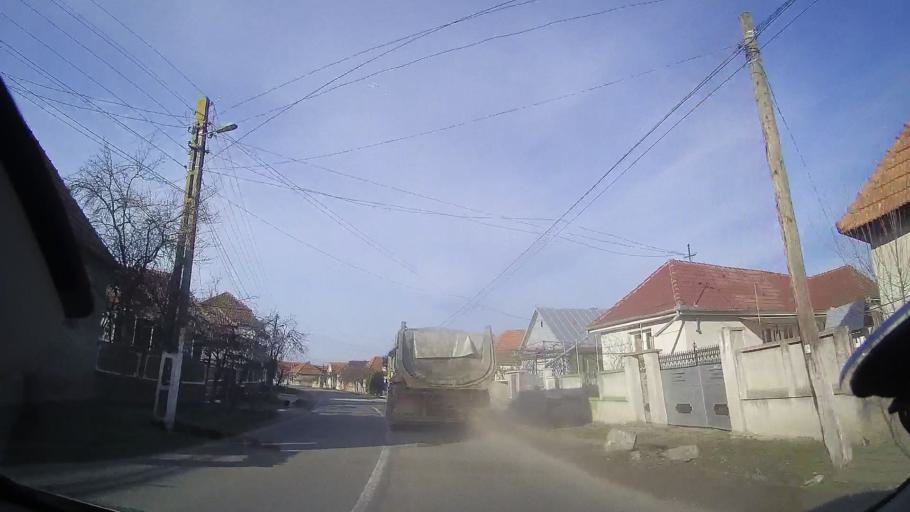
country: RO
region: Bihor
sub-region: Comuna Brusturi
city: Brusturi
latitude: 47.1414
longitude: 22.2649
